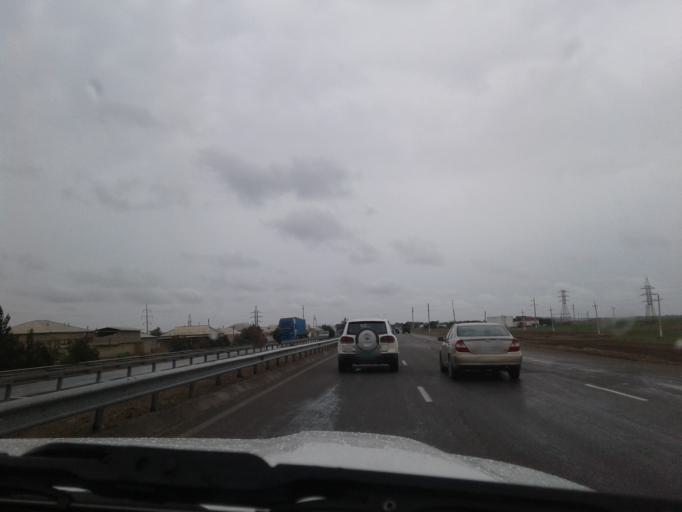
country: TM
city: Murgab
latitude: 37.6111
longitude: 61.9536
